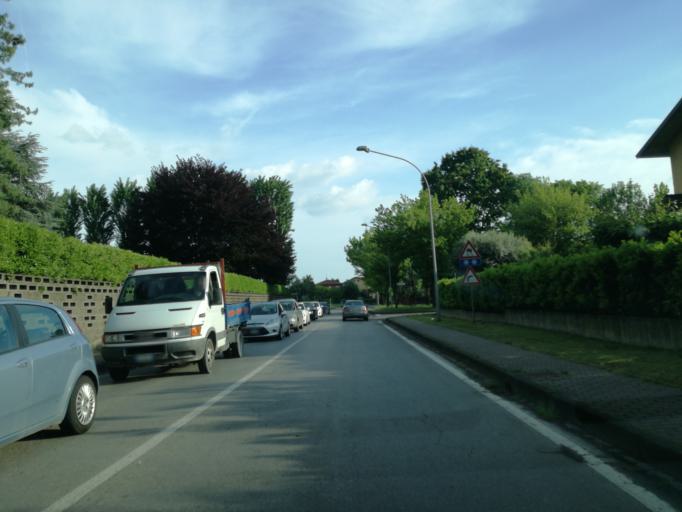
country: IT
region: Lombardy
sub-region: Provincia di Lecco
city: Paderno d'Adda
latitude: 45.6801
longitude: 9.4514
